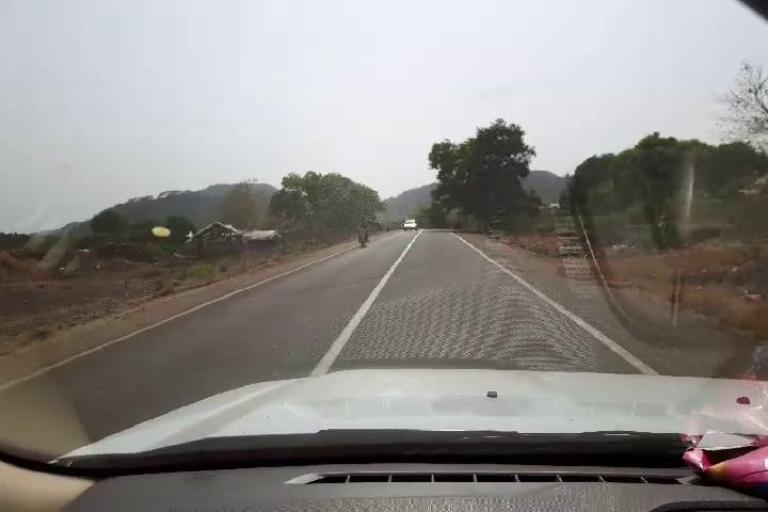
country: SL
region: Western Area
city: Waterloo
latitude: 8.2034
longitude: -13.1282
